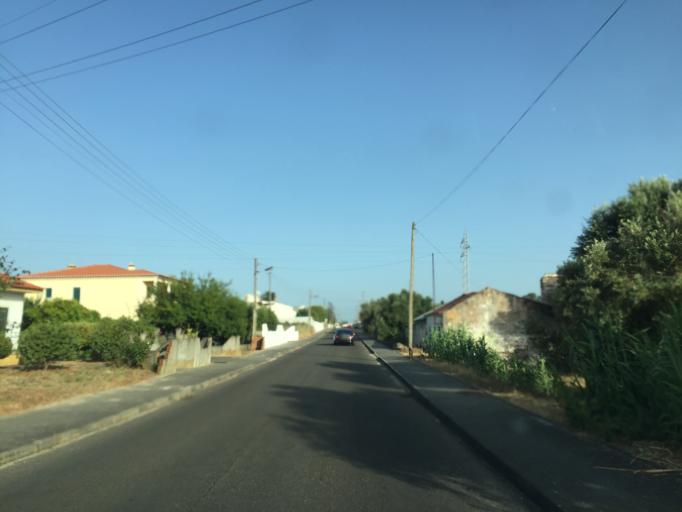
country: PT
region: Santarem
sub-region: Entroncamento
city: Entroncamento
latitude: 39.4746
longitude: -8.4485
